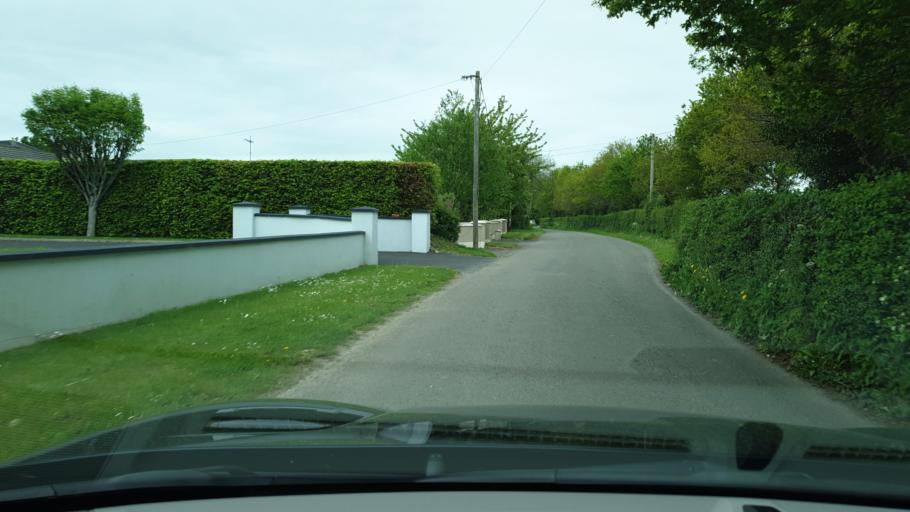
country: IE
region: Leinster
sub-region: An Mhi
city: Dunboyne
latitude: 53.4523
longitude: -6.5045
